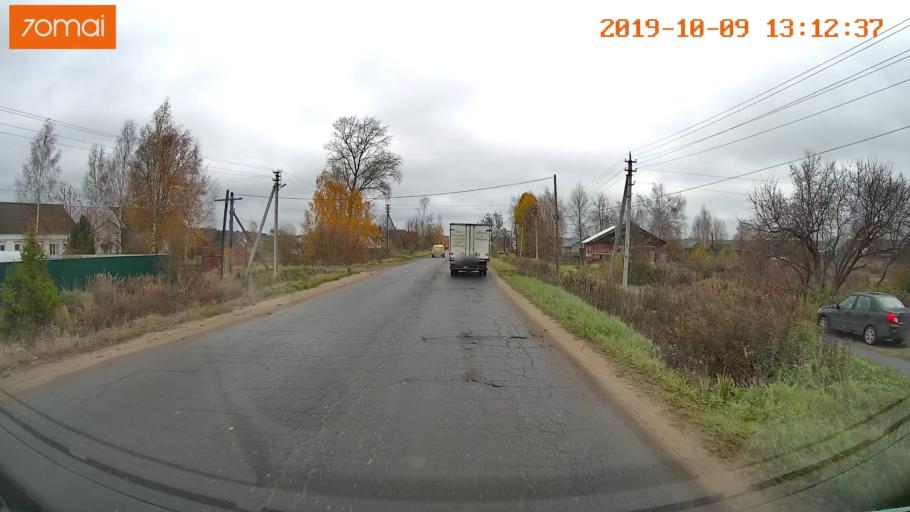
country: RU
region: Jaroslavl
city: Lyubim
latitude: 58.3616
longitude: 40.7043
